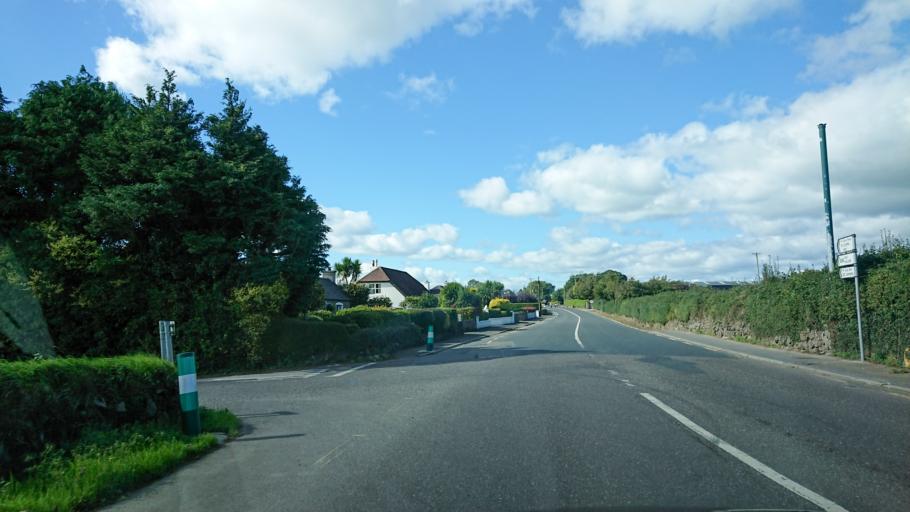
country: IE
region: Munster
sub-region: Waterford
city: Dungarvan
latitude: 52.0956
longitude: -7.6458
